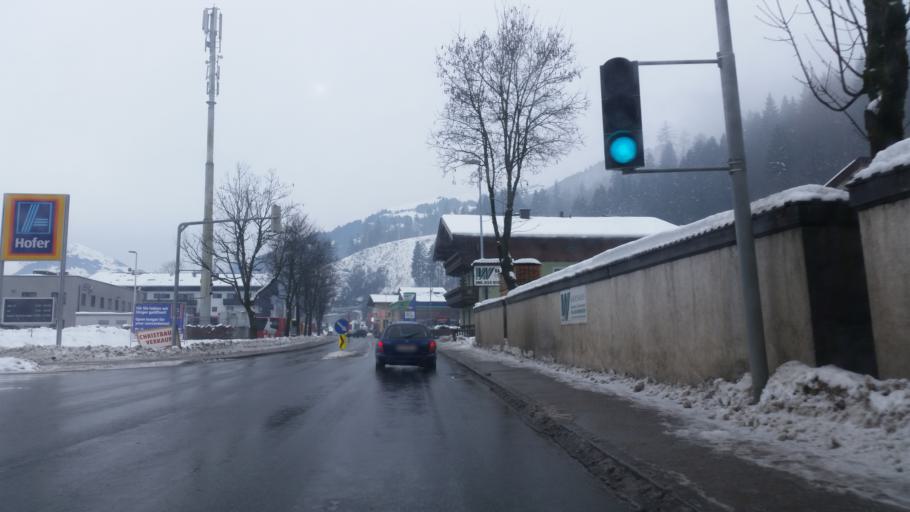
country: AT
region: Tyrol
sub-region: Politischer Bezirk Kitzbuhel
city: Kitzbuhel
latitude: 47.4573
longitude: 12.3864
